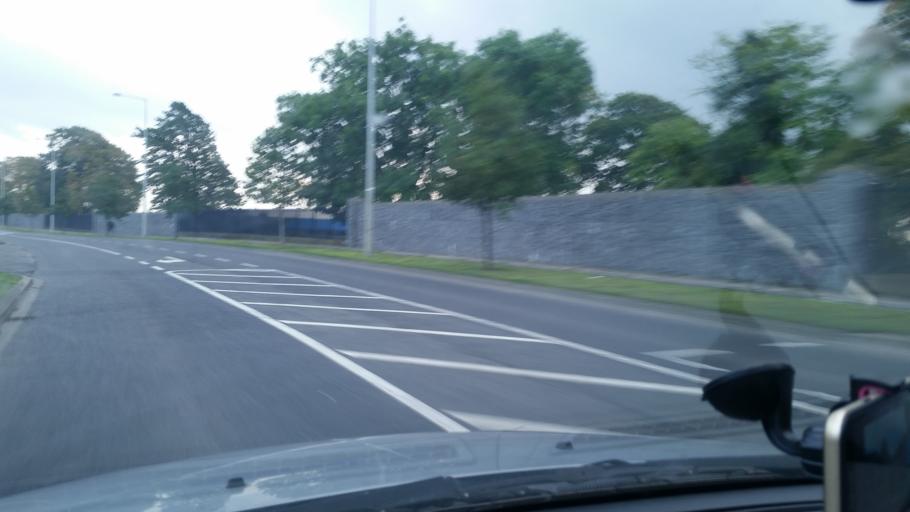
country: IE
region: Leinster
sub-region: Fingal County
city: Blanchardstown
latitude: 53.3988
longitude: -6.3517
